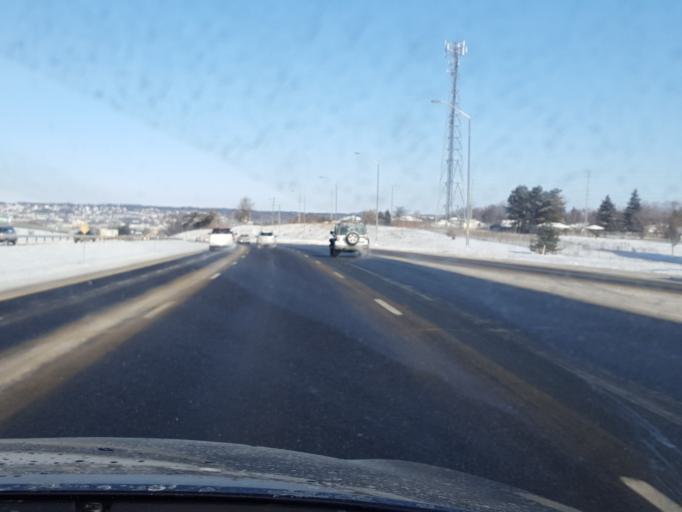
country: CA
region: Ontario
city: Barrie
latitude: 44.3539
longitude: -79.6895
